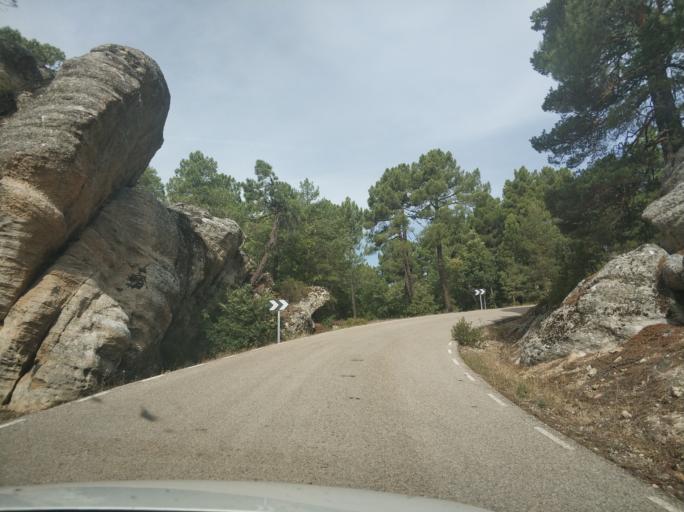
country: ES
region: Castille and Leon
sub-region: Provincia de Soria
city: Duruelo de la Sierra
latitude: 41.8944
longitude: -2.9456
